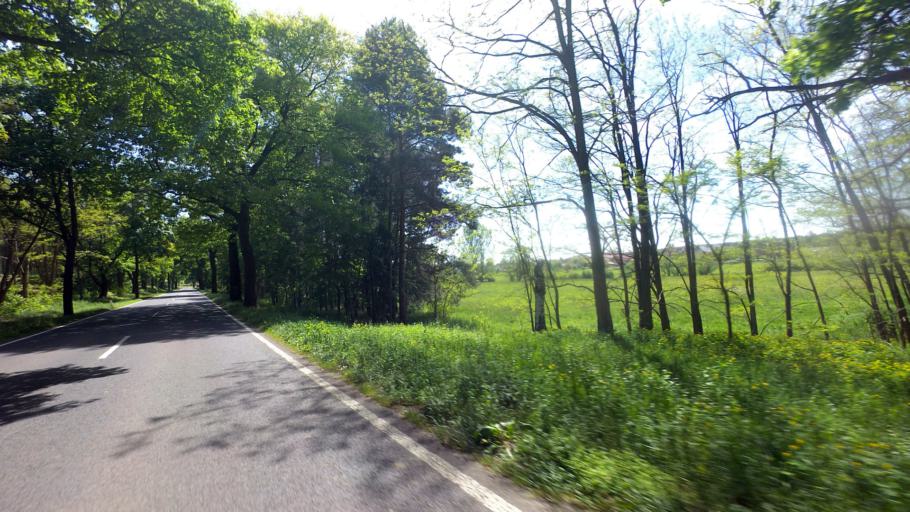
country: DE
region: Brandenburg
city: Luckenwalde
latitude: 52.1438
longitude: 13.1168
